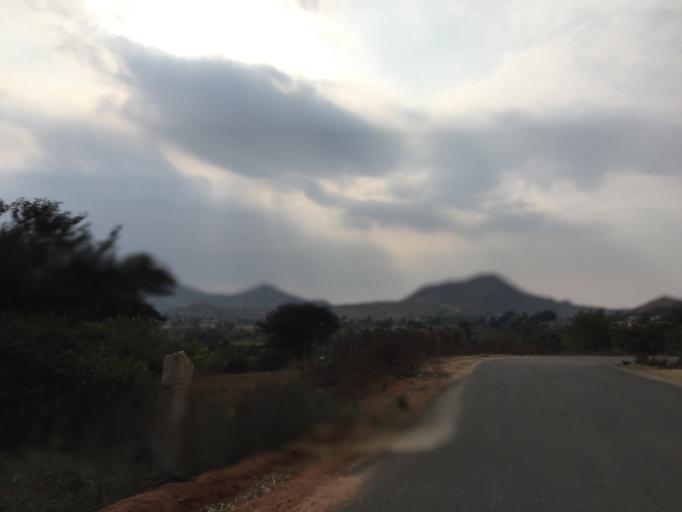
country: IN
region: Karnataka
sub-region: Chikkaballapur
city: Chik Ballapur
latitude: 13.5499
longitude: 77.7608
